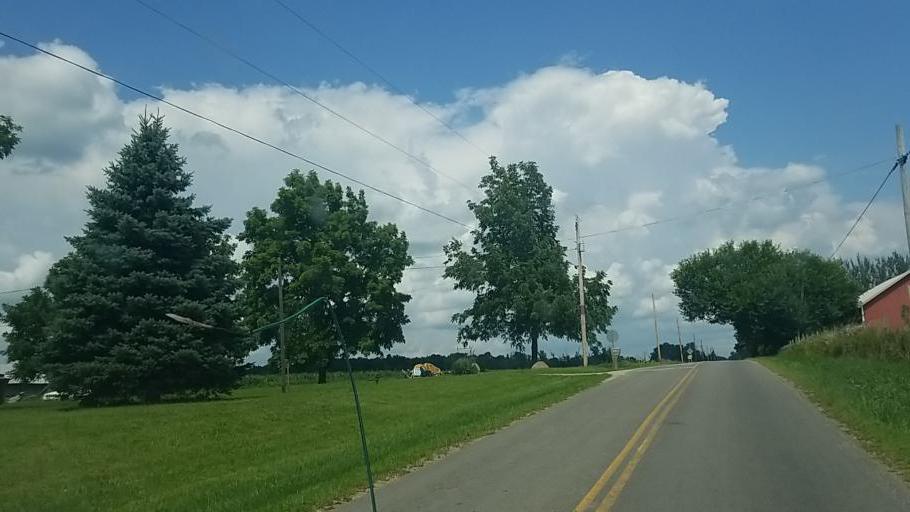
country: US
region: Ohio
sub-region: Medina County
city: Lodi
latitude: 41.0681
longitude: -82.0764
